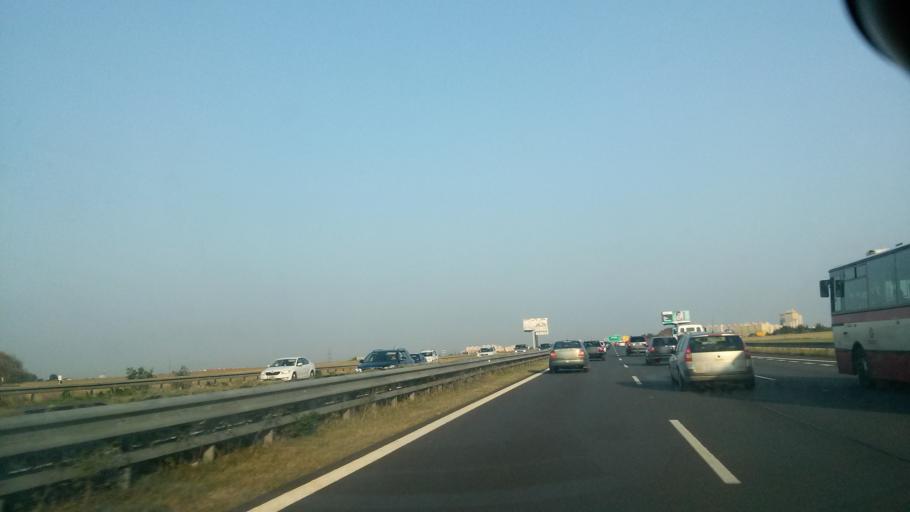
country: CZ
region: Central Bohemia
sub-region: Okres Praha-Zapad
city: Pruhonice
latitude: 50.0117
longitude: 14.5363
